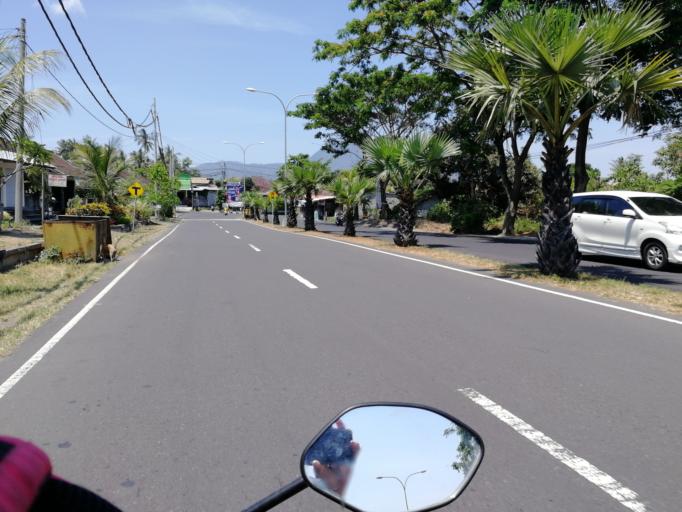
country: ID
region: Bali
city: Subagan
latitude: -8.4388
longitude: 115.5933
